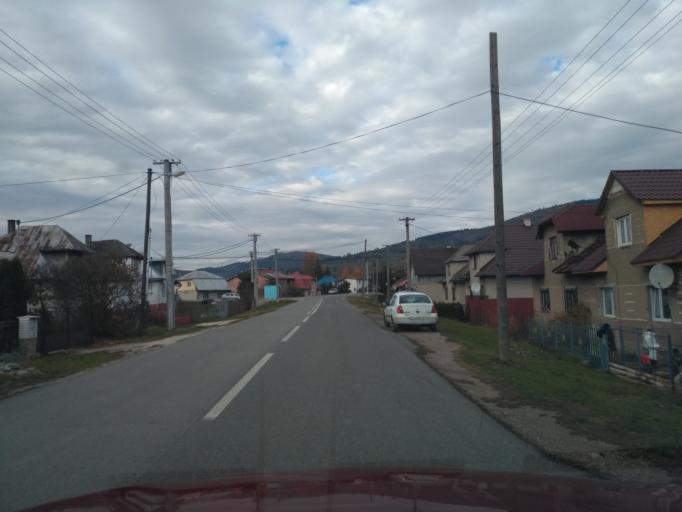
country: SK
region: Kosicky
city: Krompachy
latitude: 48.8065
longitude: 20.7258
